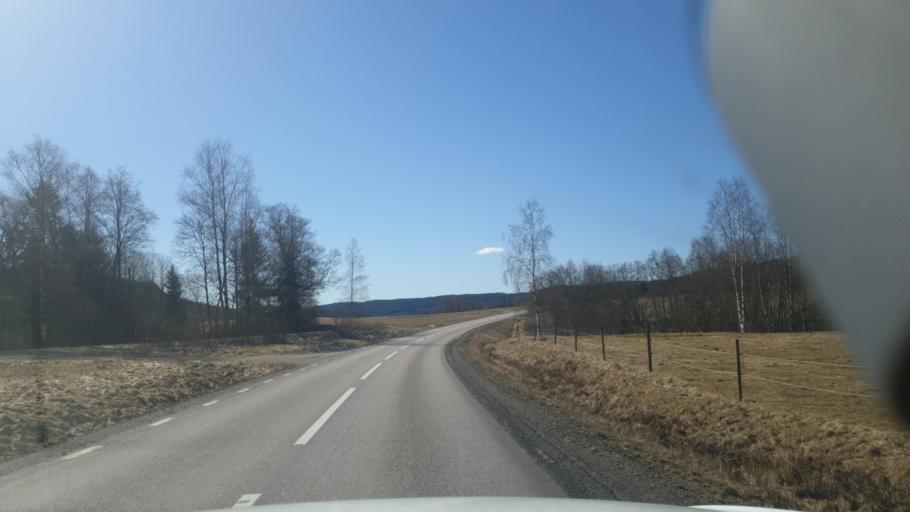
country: SE
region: Vaermland
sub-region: Eda Kommun
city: Amotfors
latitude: 59.6618
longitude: 12.1457
